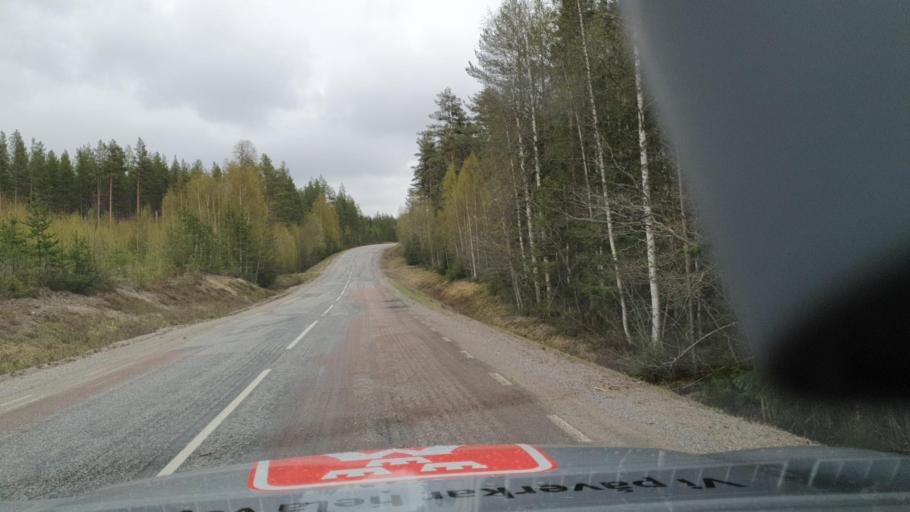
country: SE
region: Vaesterbotten
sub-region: Asele Kommun
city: Asele
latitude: 63.6925
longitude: 17.2305
